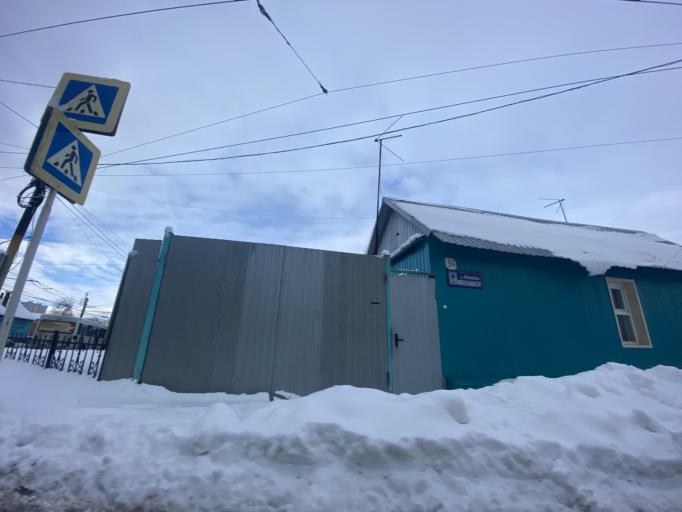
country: RU
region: Saratov
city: Engel's
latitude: 51.5012
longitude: 46.1091
